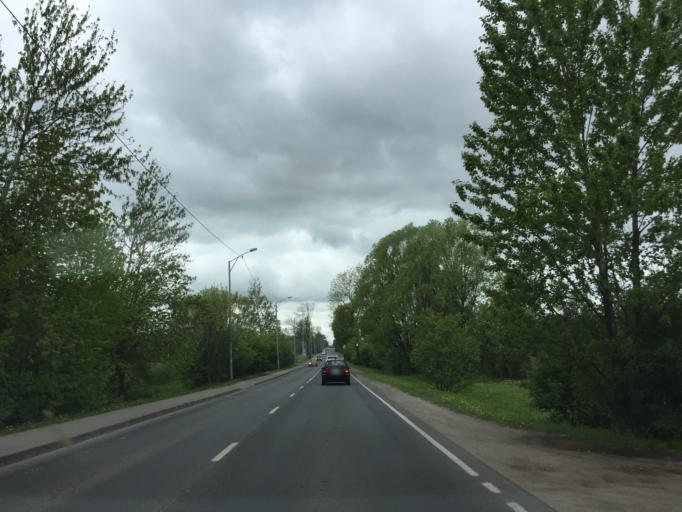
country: RU
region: Kaliningrad
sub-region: Gorod Kaliningrad
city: Kaliningrad
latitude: 54.6757
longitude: 20.4413
